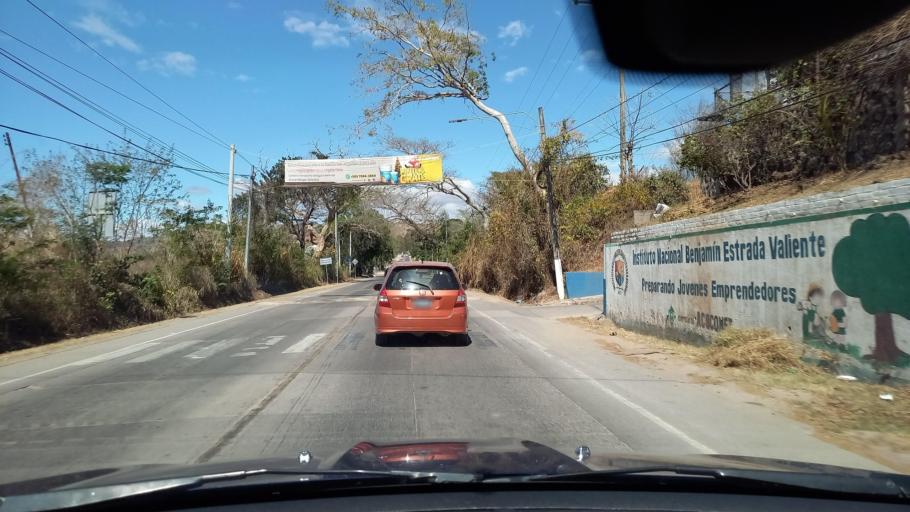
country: SV
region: Santa Ana
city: Metapan
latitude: 14.3387
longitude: -89.4492
